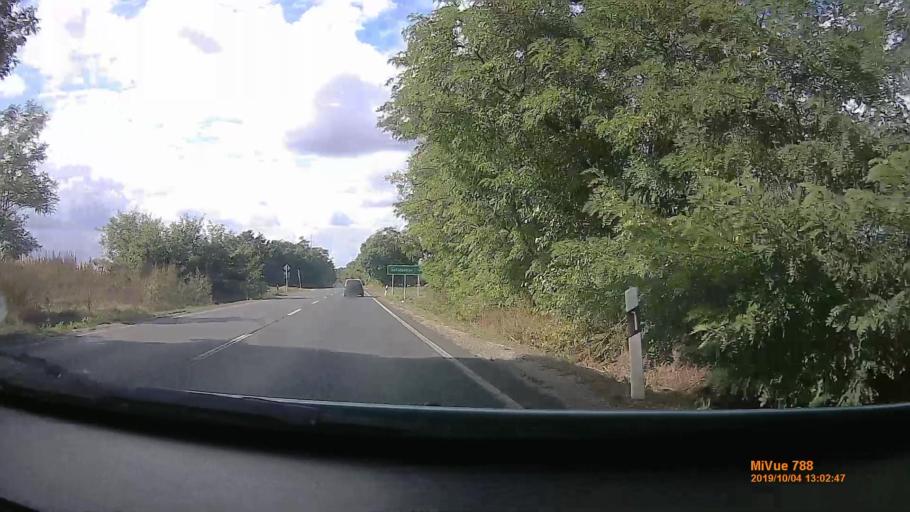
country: HU
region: Szabolcs-Szatmar-Bereg
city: Nyirtelek
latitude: 47.9574
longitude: 21.6465
